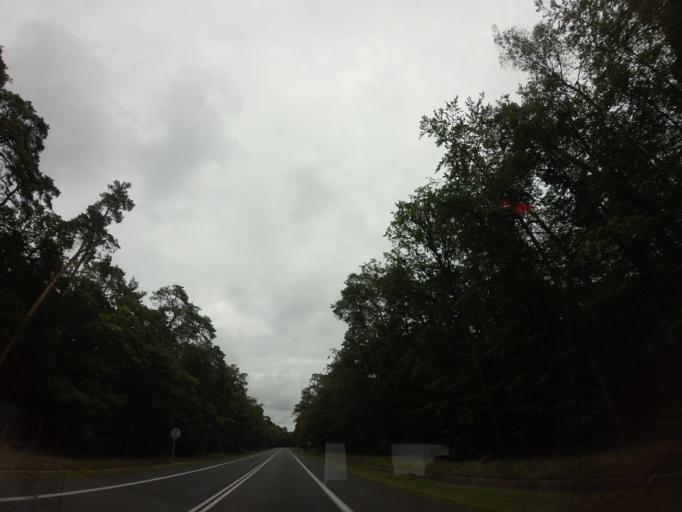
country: PL
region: West Pomeranian Voivodeship
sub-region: Powiat kamienski
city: Miedzyzdroje
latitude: 53.9018
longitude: 14.4522
